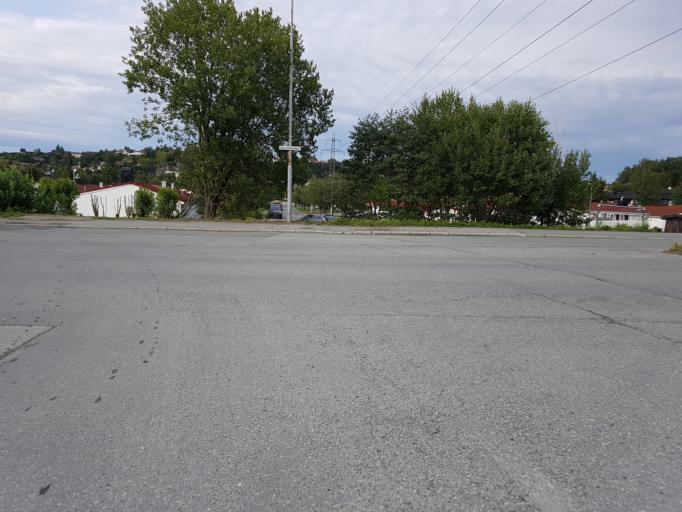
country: NO
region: Sor-Trondelag
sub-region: Trondheim
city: Trondheim
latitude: 63.4017
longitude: 10.4290
